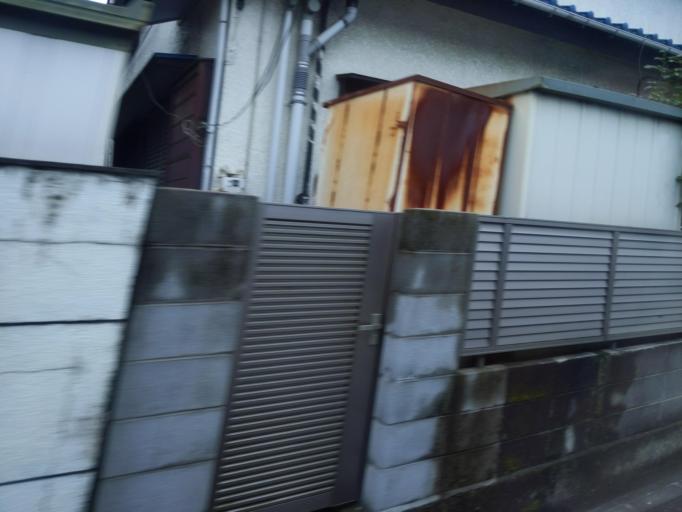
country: JP
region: Tokyo
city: Chofugaoka
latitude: 35.6111
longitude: 139.5717
